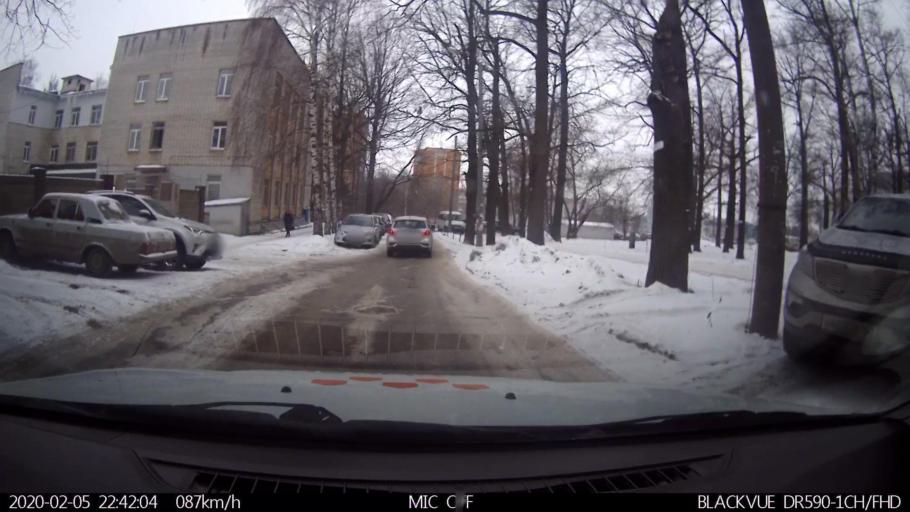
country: RU
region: Nizjnij Novgorod
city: Imeni Stepana Razina
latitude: 54.7190
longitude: 44.3494
